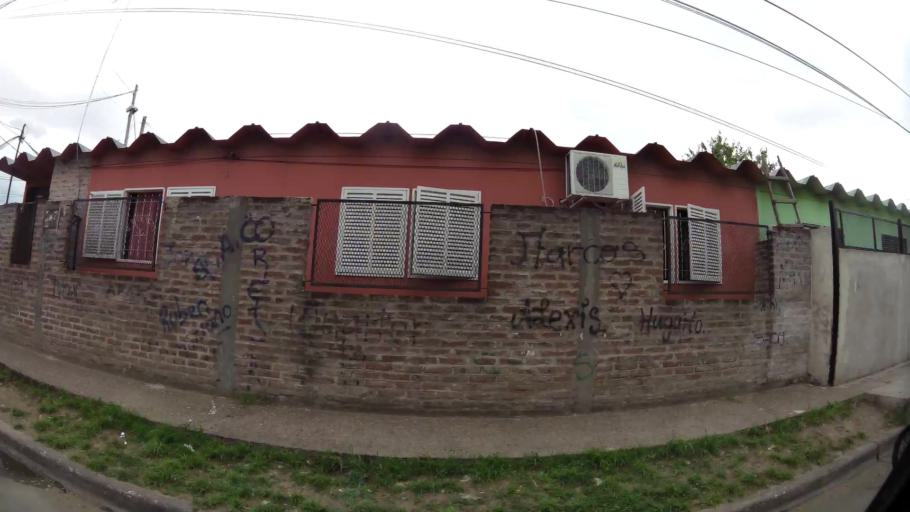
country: AR
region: Buenos Aires
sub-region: Partido de Quilmes
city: Quilmes
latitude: -34.7534
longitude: -58.2506
